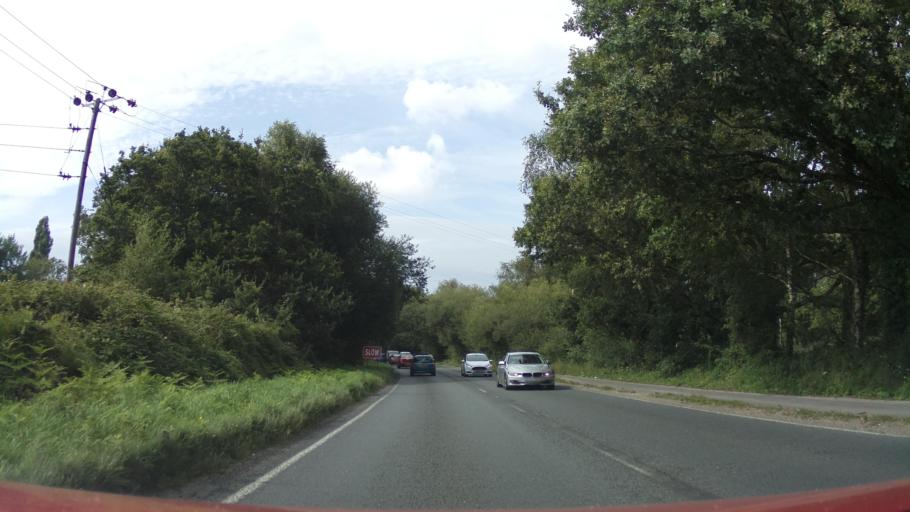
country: GB
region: England
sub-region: Hampshire
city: Marchwood
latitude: 50.8708
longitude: -1.4390
